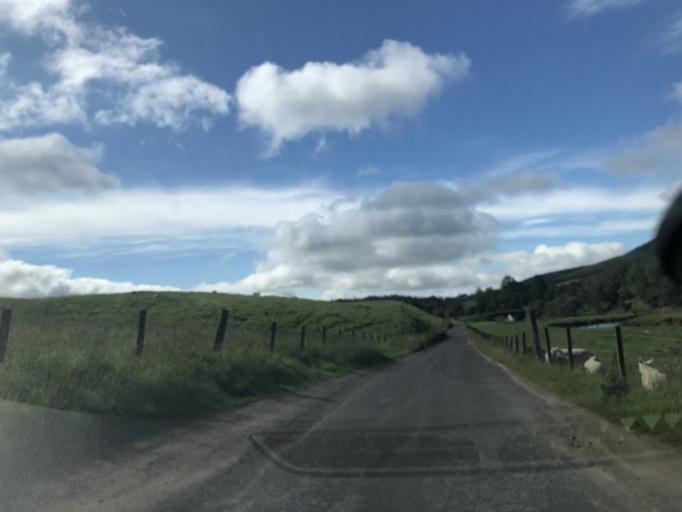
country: GB
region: Scotland
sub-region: Angus
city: Kirriemuir
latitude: 56.7782
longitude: -3.0280
